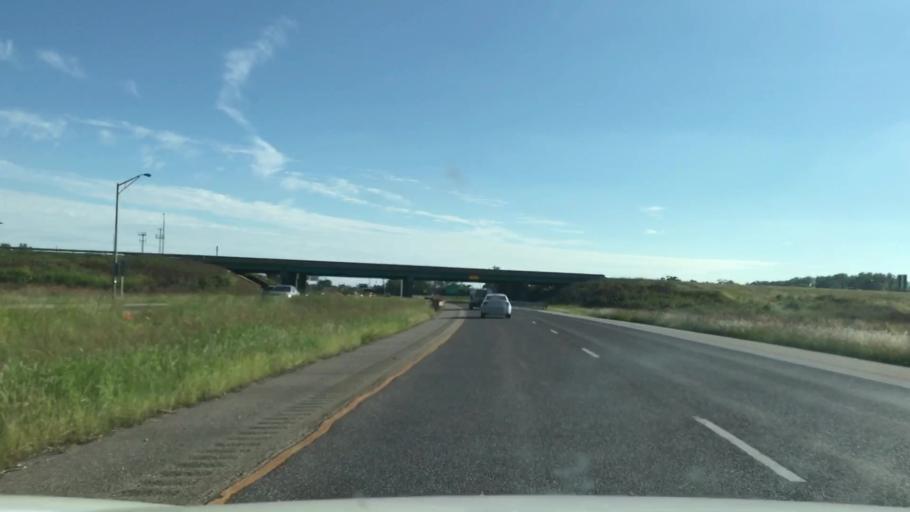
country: US
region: Illinois
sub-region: Madison County
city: Mitchell
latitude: 38.7676
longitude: -90.1237
